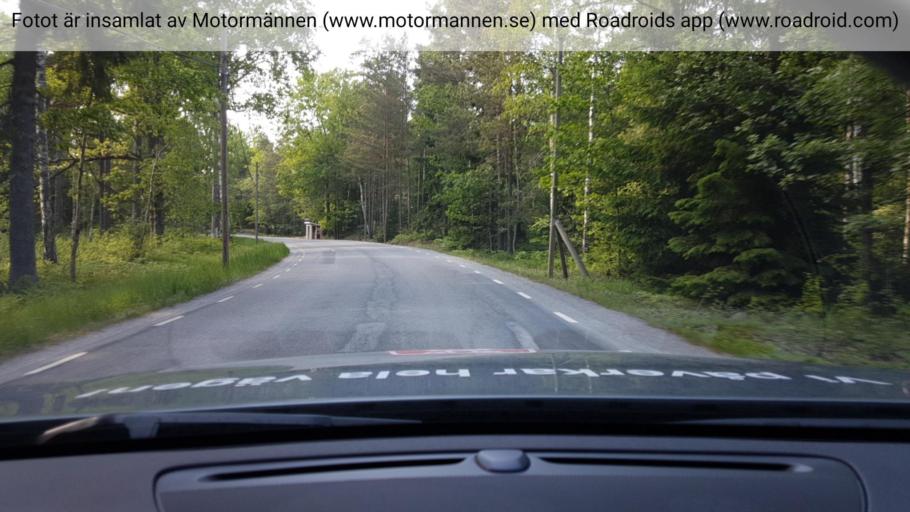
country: SE
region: Stockholm
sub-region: Varmdo Kommun
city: Mortnas
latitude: 59.2643
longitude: 18.4326
